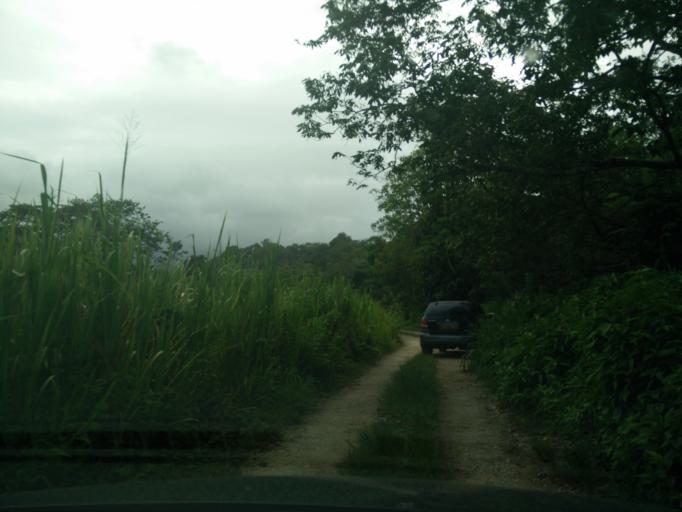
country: GP
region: Guadeloupe
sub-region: Guadeloupe
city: Capesterre-Belle-Eau
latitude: 16.1112
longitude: -61.6039
